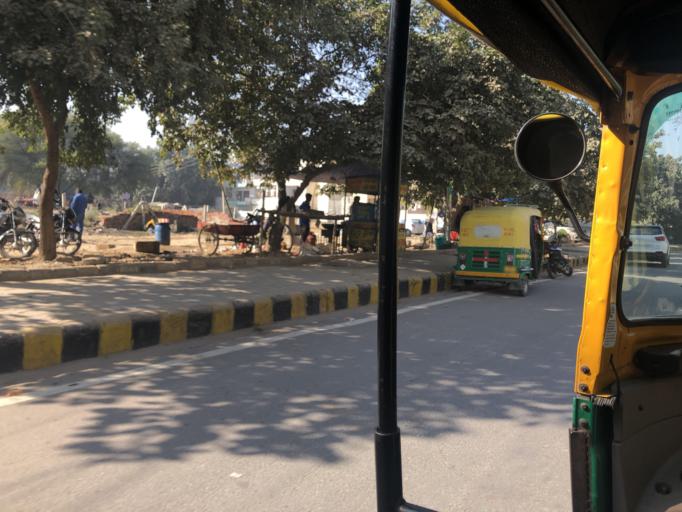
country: IN
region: Haryana
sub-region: Gurgaon
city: Gurgaon
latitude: 28.4498
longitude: 77.0701
